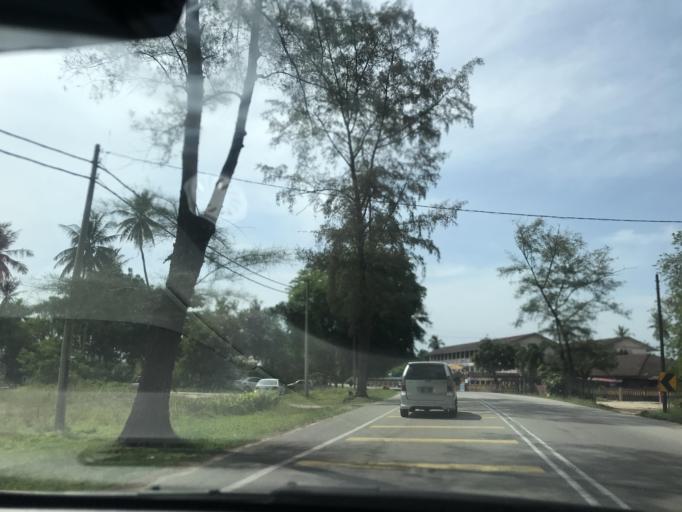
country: MY
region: Kelantan
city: Tumpat
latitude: 6.2109
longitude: 102.1330
